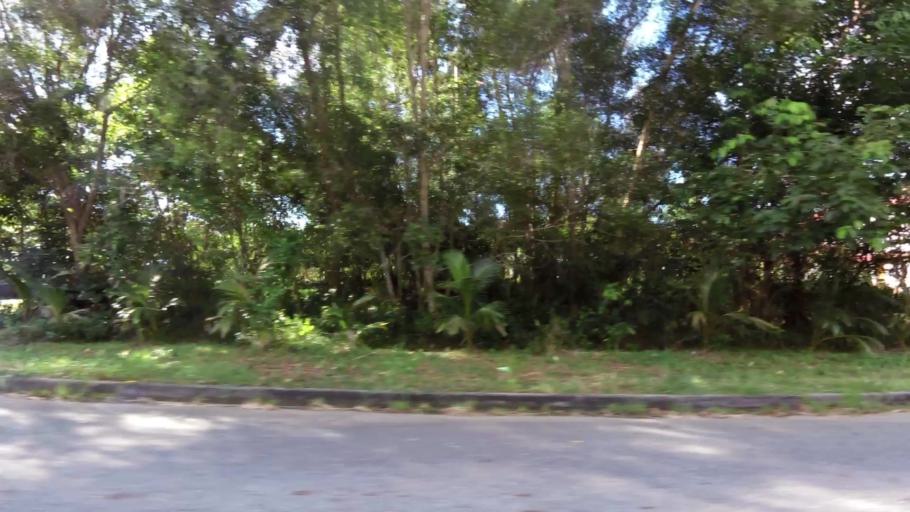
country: BN
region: Brunei and Muara
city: Bandar Seri Begawan
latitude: 4.9770
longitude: 114.9703
